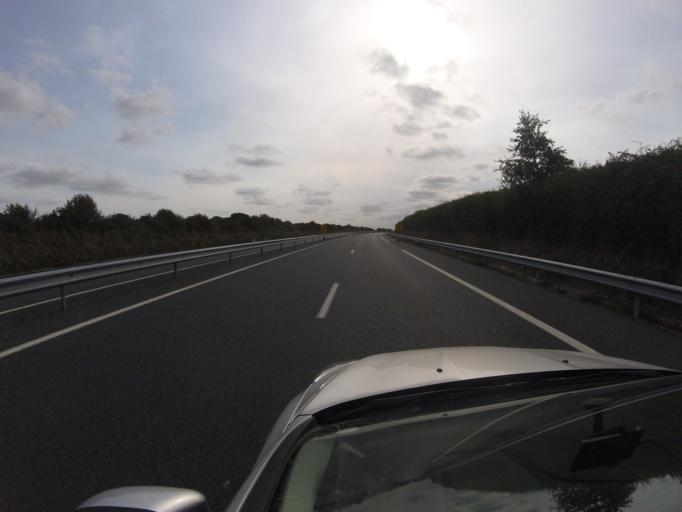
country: FR
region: Lower Normandy
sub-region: Departement de la Manche
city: Pont-Hebert
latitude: 49.1498
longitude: -1.1590
